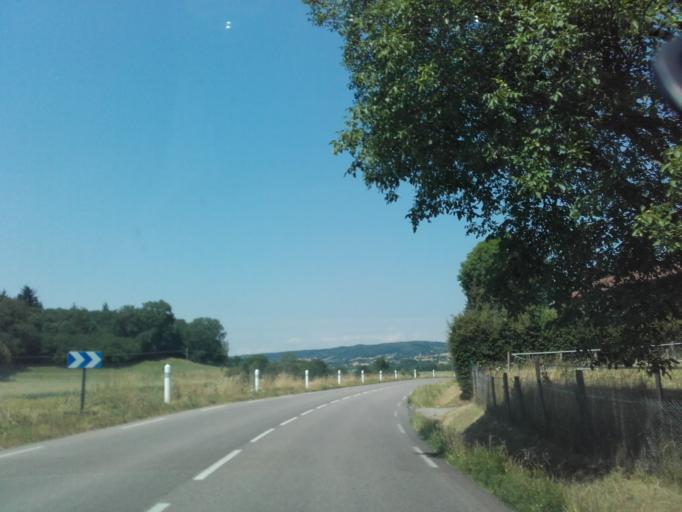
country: FR
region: Rhone-Alpes
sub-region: Departement de l'Isere
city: La Cote-Saint-Andre
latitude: 45.4125
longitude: 5.2616
